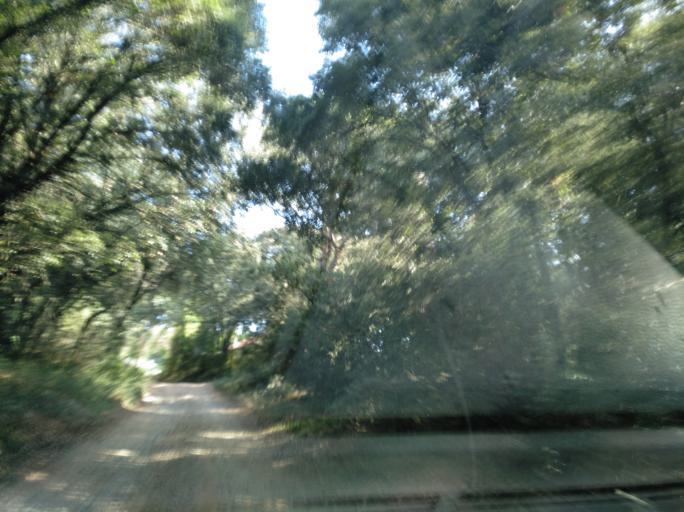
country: ES
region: Catalonia
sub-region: Provincia de Girona
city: la Cellera de Ter
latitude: 42.0043
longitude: 2.6324
